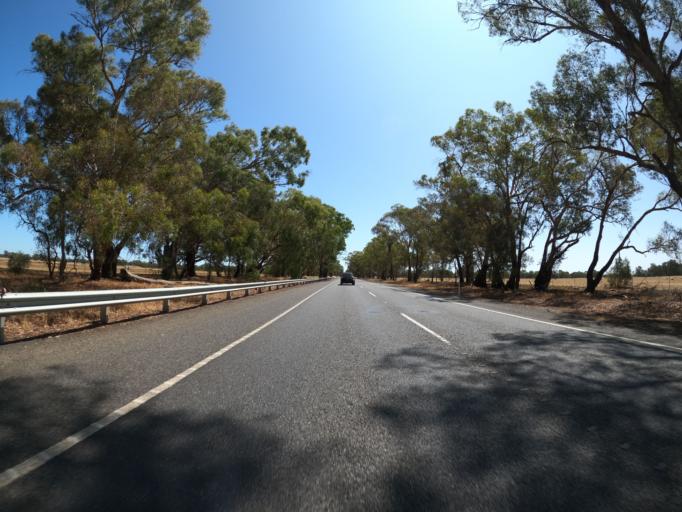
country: AU
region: New South Wales
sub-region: Corowa Shire
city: Corowa
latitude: -36.0603
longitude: 146.4163
